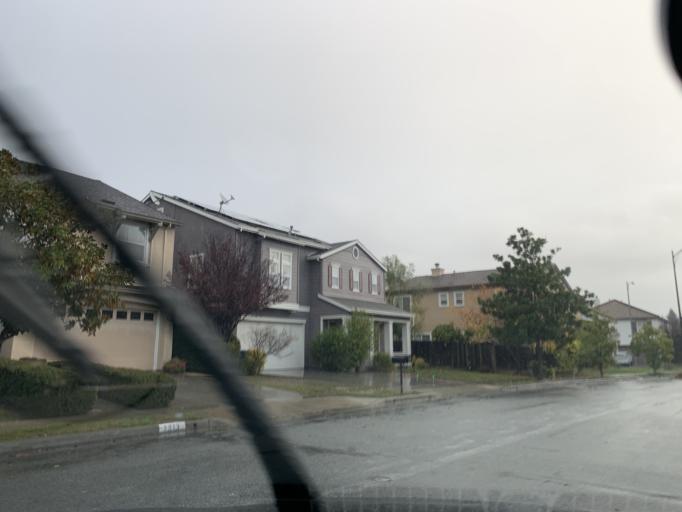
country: US
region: California
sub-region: Santa Clara County
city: Cambrian Park
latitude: 37.2541
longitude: -121.9420
